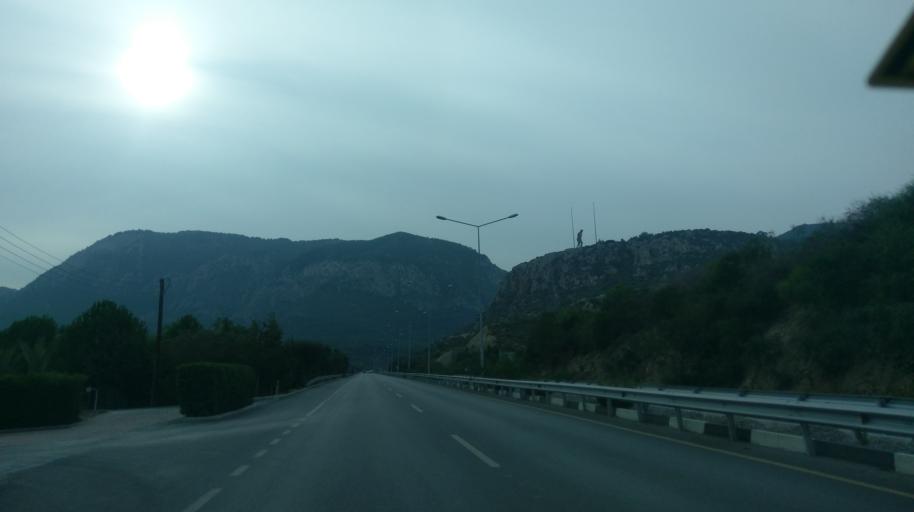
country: CY
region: Keryneia
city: Kyrenia
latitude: 35.3180
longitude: 33.3219
